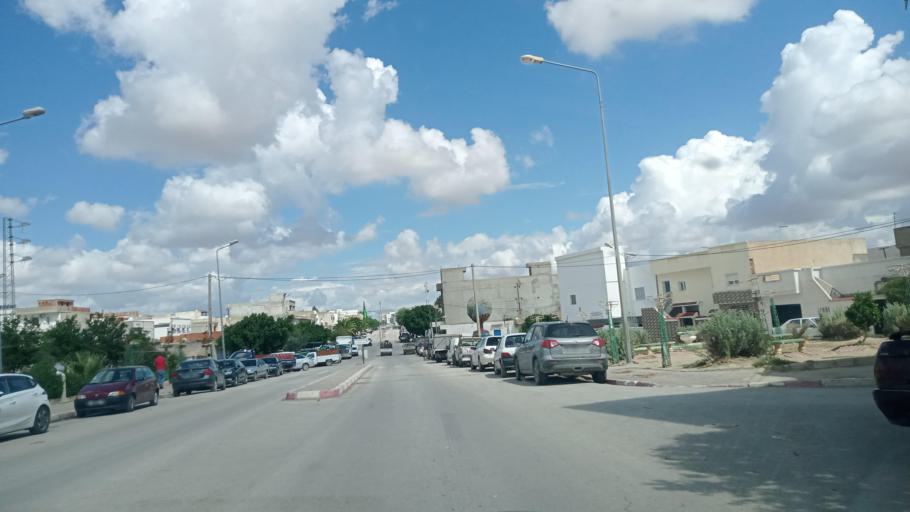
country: TN
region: Silyanah
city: Al Karib
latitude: 36.3242
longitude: 9.1313
